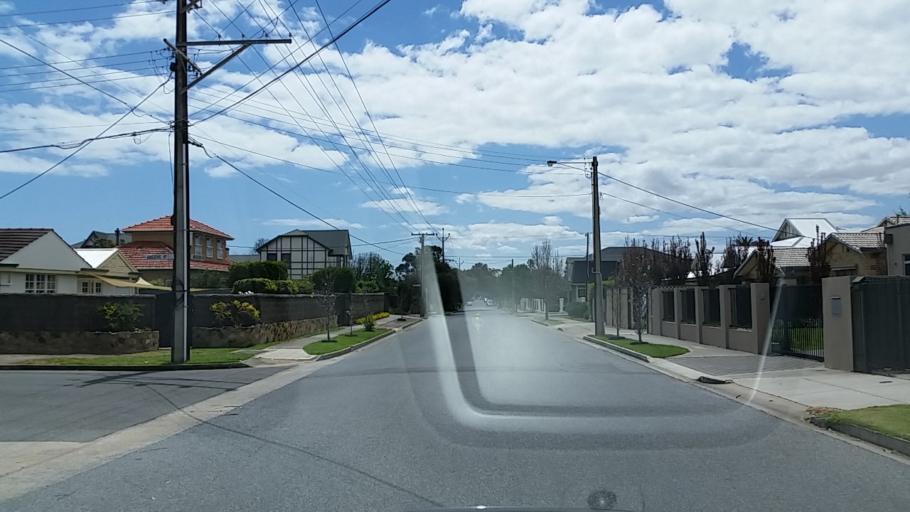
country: AU
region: South Australia
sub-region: Holdfast Bay
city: North Brighton
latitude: -34.9953
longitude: 138.5162
